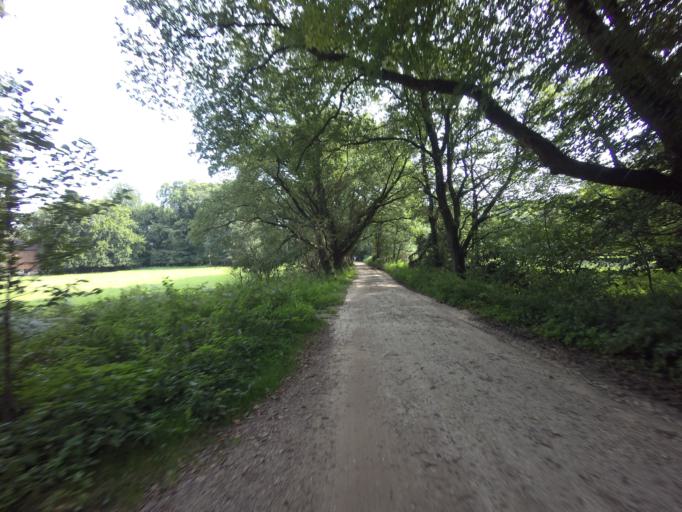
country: DE
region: Lower Saxony
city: Getelo
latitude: 52.4331
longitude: 6.8953
